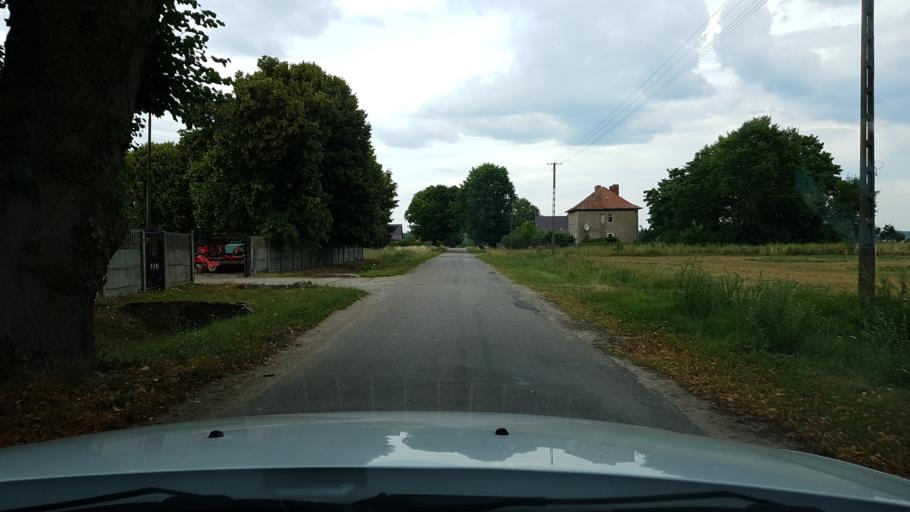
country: PL
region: West Pomeranian Voivodeship
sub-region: Powiat walecki
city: Walcz
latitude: 53.3930
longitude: 16.3335
